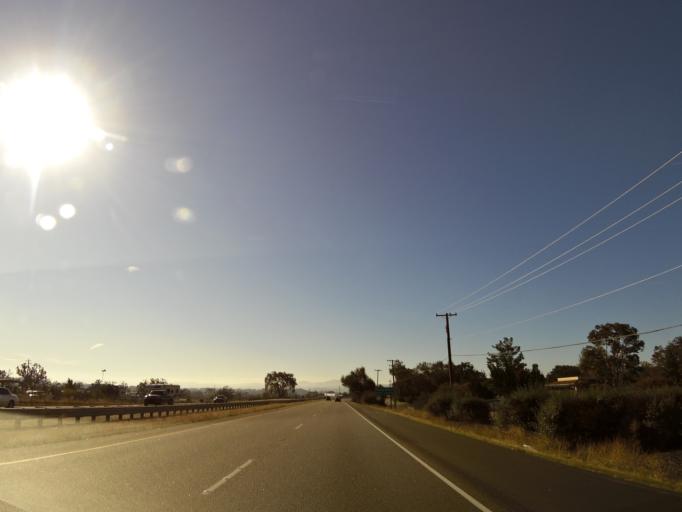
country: US
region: California
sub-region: San Luis Obispo County
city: Templeton
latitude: 35.5775
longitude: -120.6973
